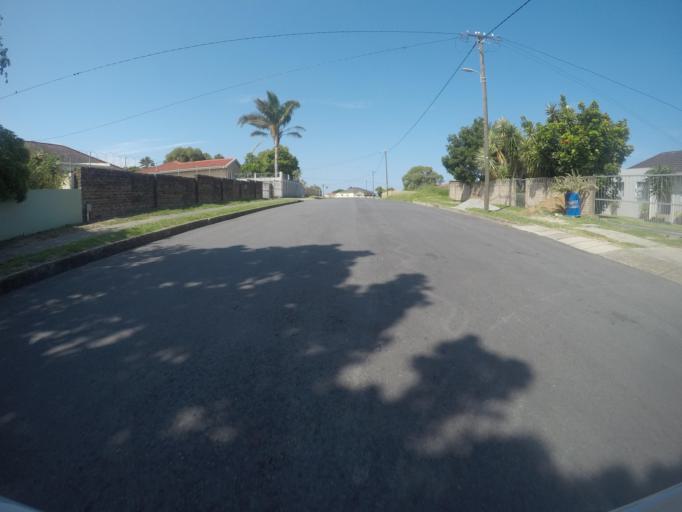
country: ZA
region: Eastern Cape
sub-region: Buffalo City Metropolitan Municipality
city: East London
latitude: -32.9799
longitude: 27.8741
